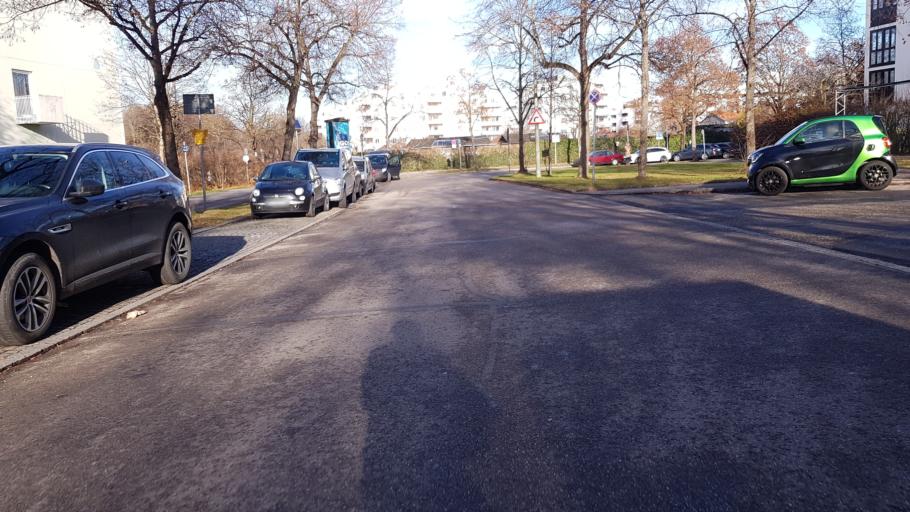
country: DE
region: Bavaria
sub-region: Upper Bavaria
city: Munich
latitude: 48.1211
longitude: 11.5315
